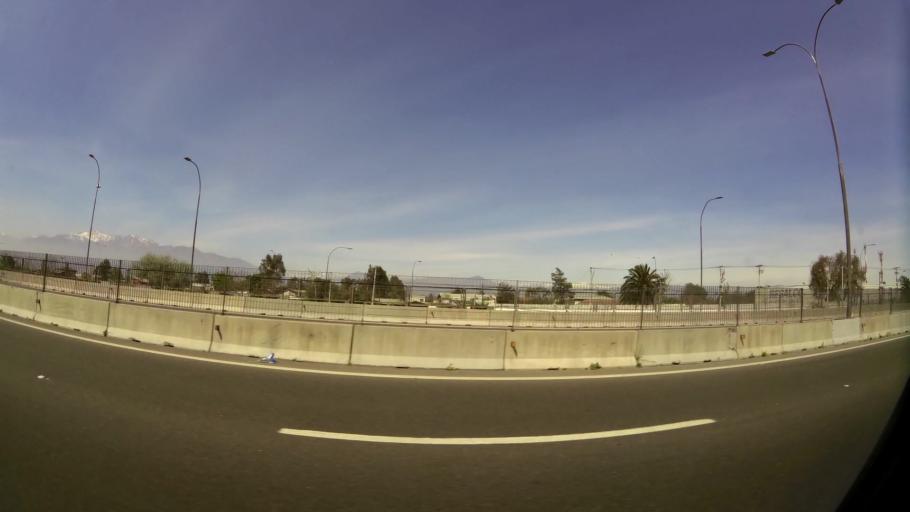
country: CL
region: Santiago Metropolitan
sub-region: Provincia de Maipo
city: San Bernardo
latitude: -33.5405
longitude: -70.6862
